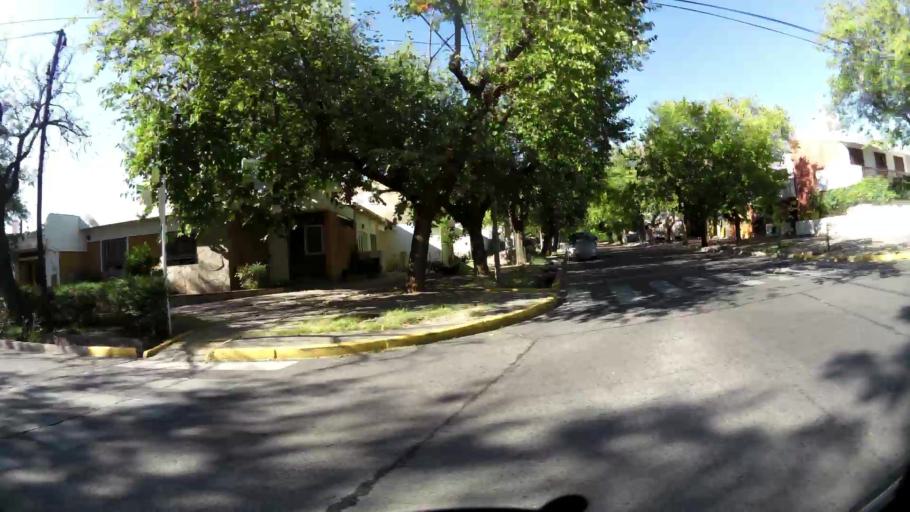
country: AR
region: Mendoza
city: Las Heras
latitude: -32.8705
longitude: -68.8548
